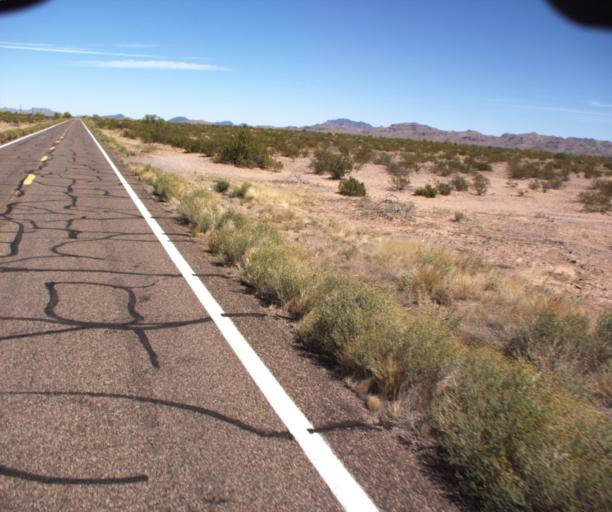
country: US
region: Arizona
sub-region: Pima County
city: Ajo
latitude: 32.6207
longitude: -112.8667
